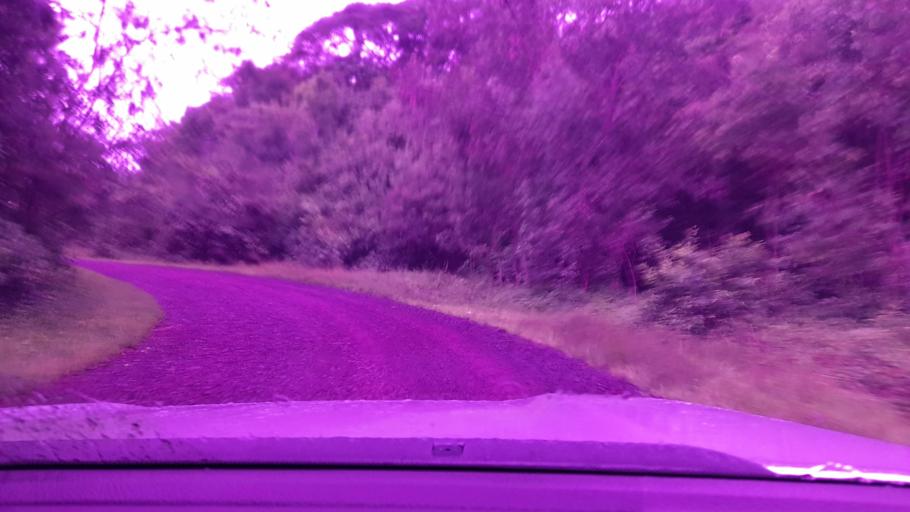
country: ET
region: Oromiya
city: Metu
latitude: 8.4544
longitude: 35.6384
